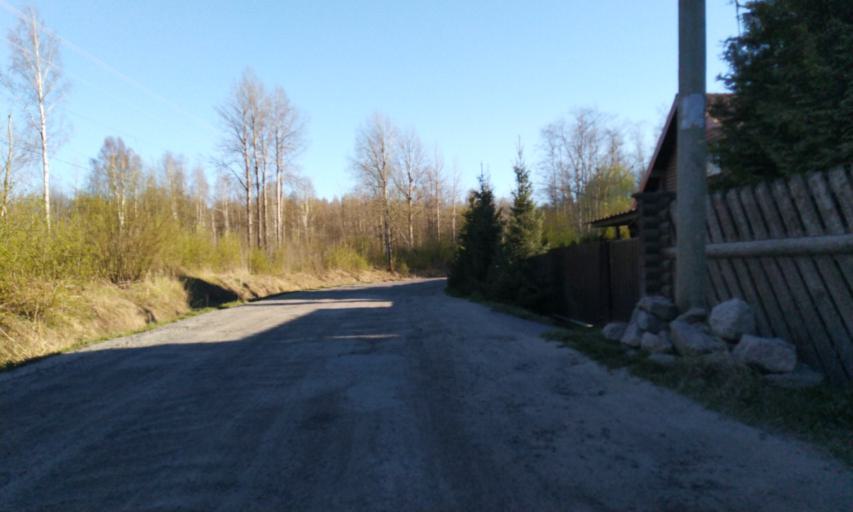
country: RU
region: Leningrad
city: Toksovo
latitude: 60.1491
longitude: 30.5808
